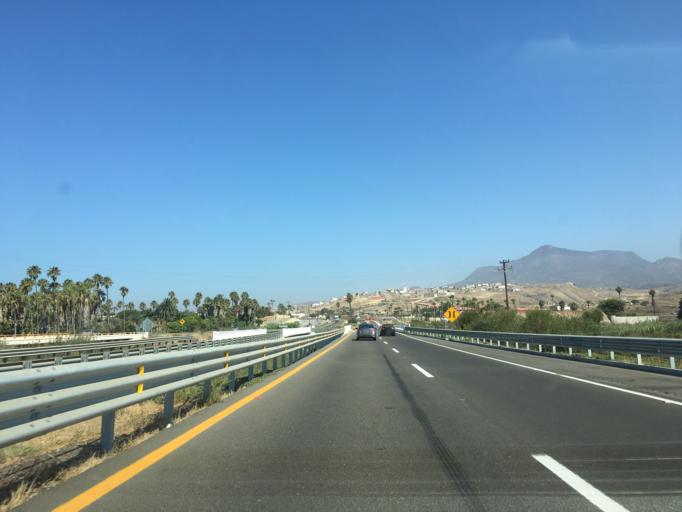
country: MX
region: Baja California
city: Primo Tapia
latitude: 32.2292
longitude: -116.9205
